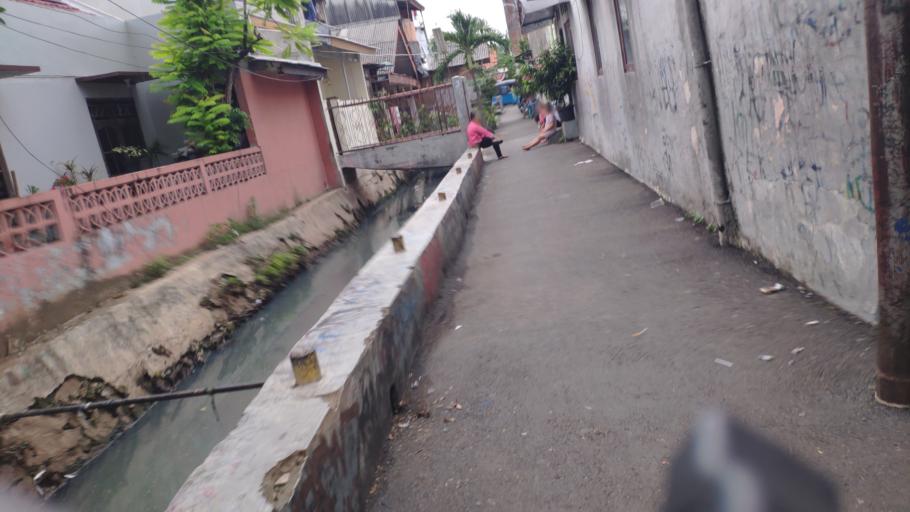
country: ID
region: Jakarta Raya
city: Jakarta
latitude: -6.2196
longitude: 106.8421
